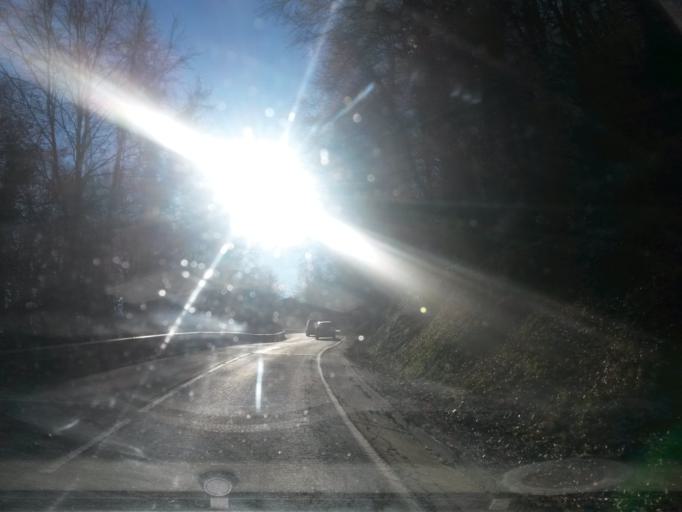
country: ES
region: Catalonia
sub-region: Provincia de Girona
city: Sant Feliu de Pallerols
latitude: 42.0505
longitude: 2.5094
